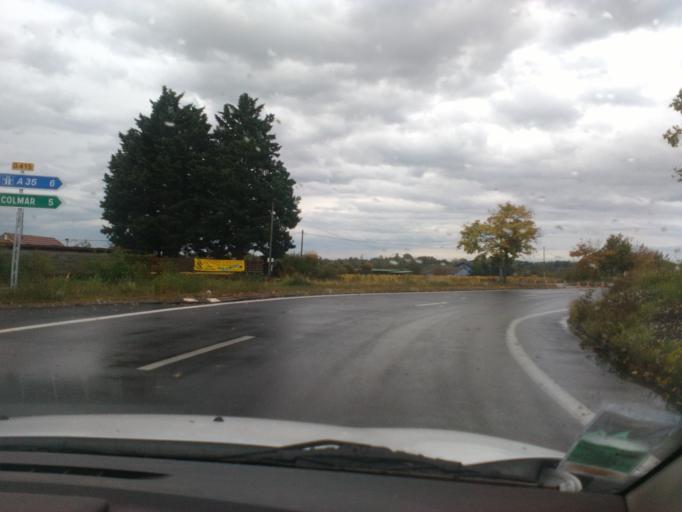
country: FR
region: Alsace
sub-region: Departement du Haut-Rhin
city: Ingersheim
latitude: 48.1035
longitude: 7.3032
